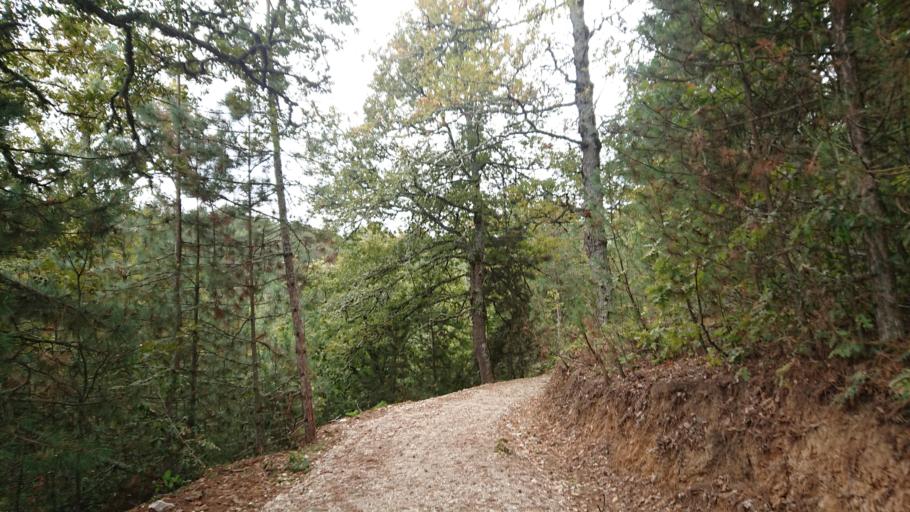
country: TR
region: Bilecik
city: Pazaryeri
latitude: 40.0156
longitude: 29.7954
